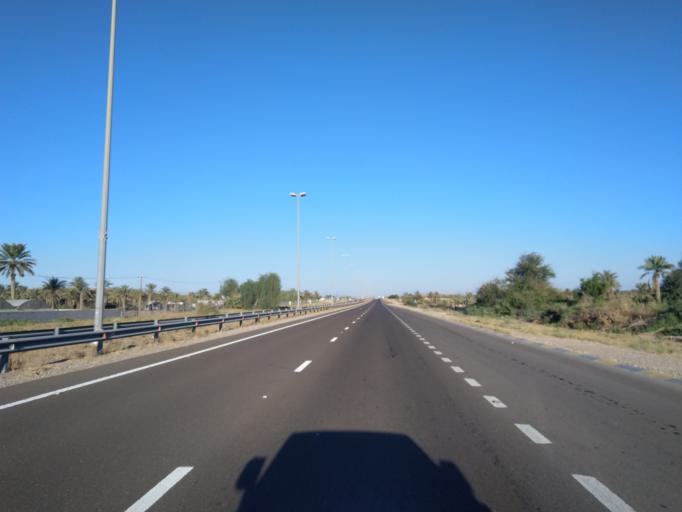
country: OM
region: Al Buraimi
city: Al Buraymi
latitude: 24.5454
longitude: 55.6583
